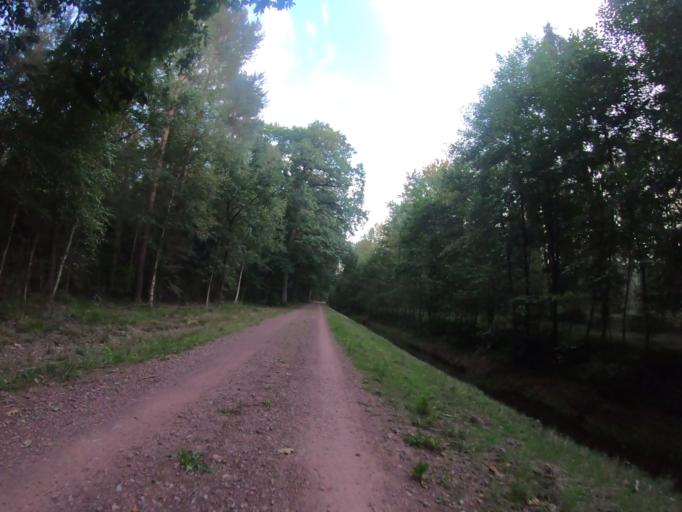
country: DE
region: Lower Saxony
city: Gifhorn
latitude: 52.5209
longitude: 10.5616
